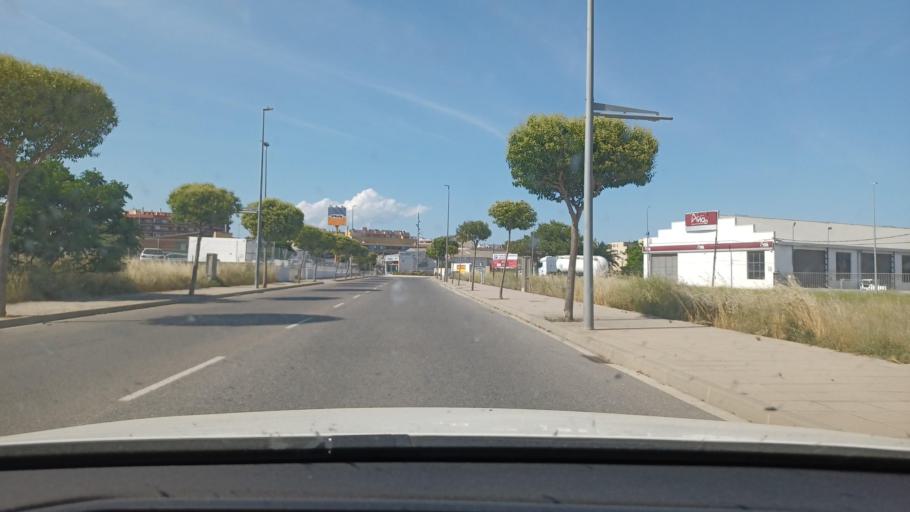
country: ES
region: Catalonia
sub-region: Provincia de Tarragona
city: Amposta
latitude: 40.6995
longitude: 0.5798
